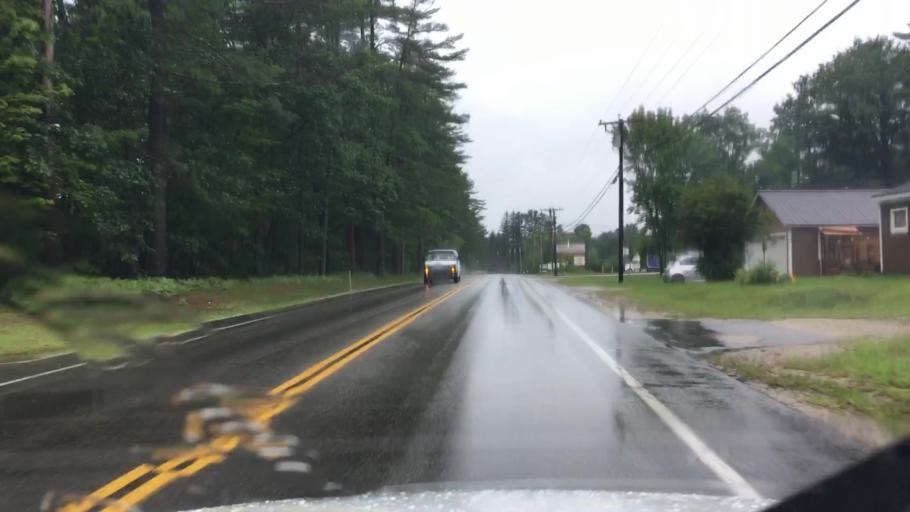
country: US
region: New Hampshire
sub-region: Carroll County
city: Conway
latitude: 43.9928
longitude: -71.0518
